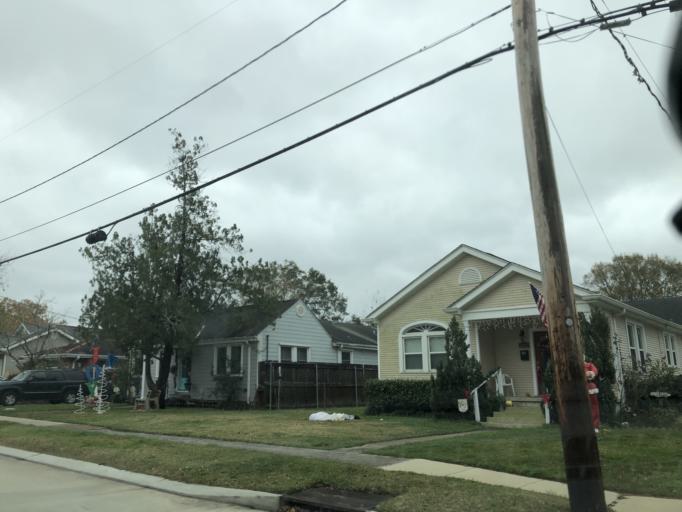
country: US
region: Louisiana
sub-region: Jefferson Parish
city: Metairie Terrace
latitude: 29.9807
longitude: -90.1615
